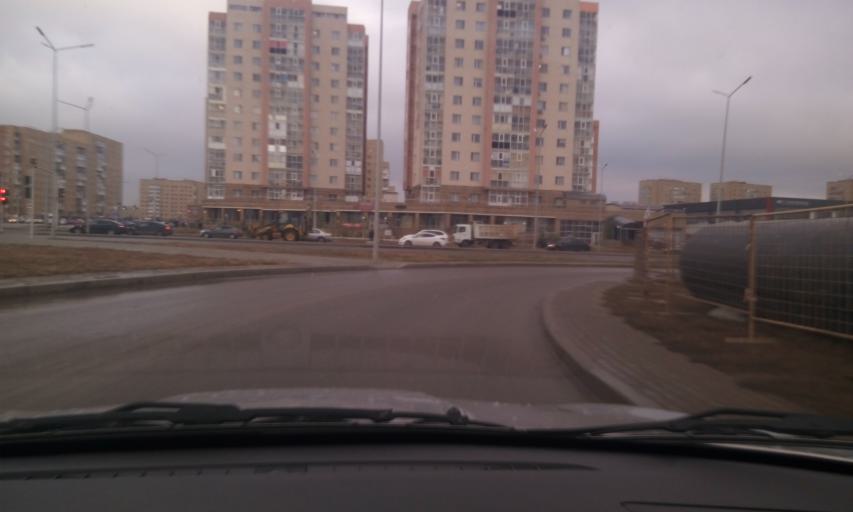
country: KZ
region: Astana Qalasy
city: Astana
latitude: 51.1718
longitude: 71.3762
